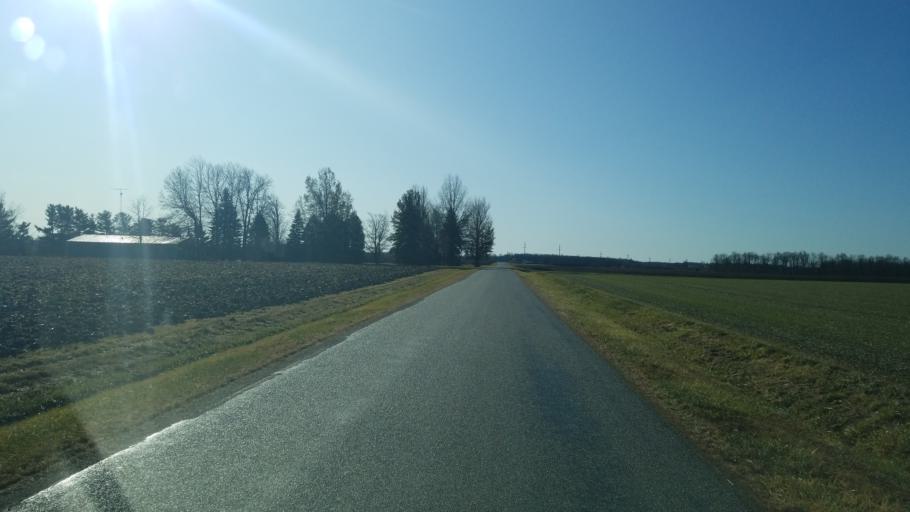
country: US
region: Ohio
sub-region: Crawford County
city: Crestline
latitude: 40.8302
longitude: -82.7060
